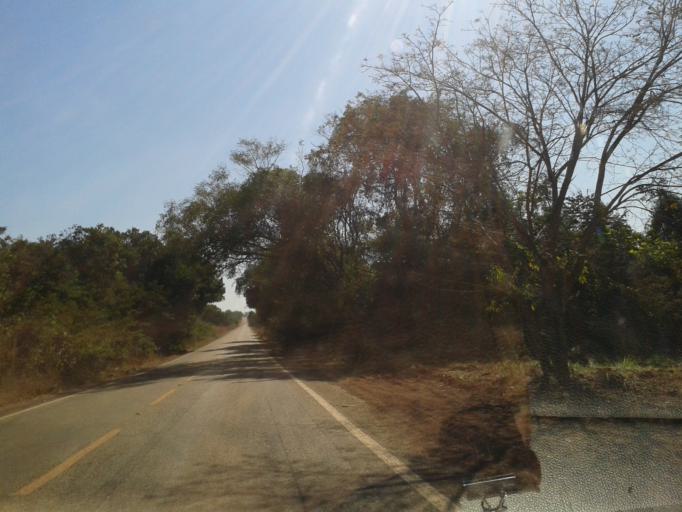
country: BR
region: Goias
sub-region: Mozarlandia
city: Mozarlandia
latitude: -14.4072
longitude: -50.4453
